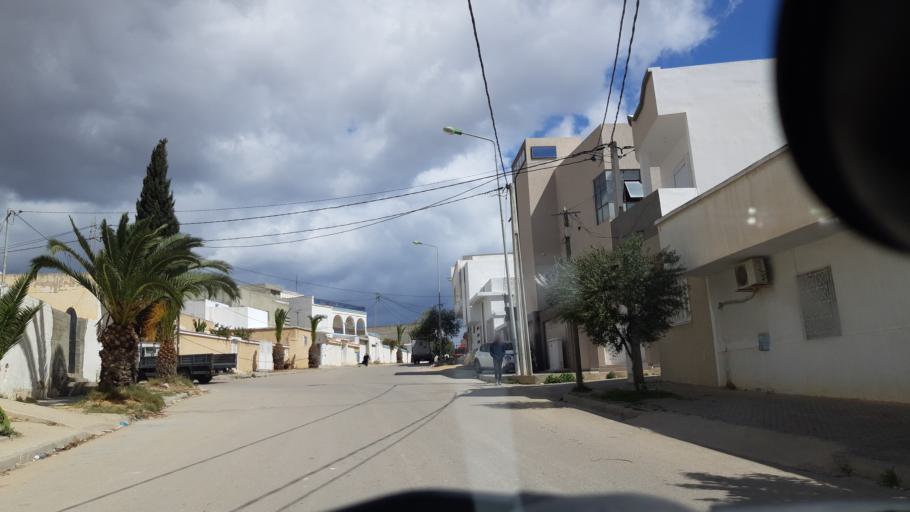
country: TN
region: Susah
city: Akouda
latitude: 35.8768
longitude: 10.5423
